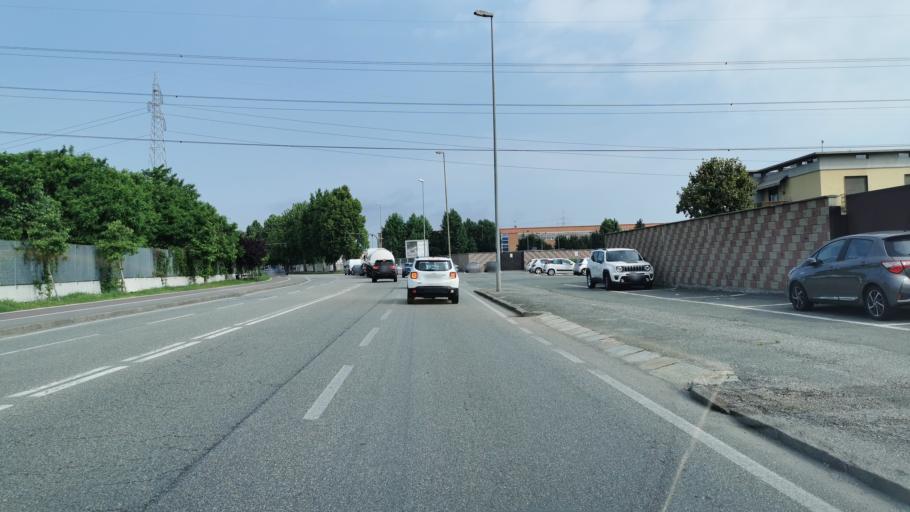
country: IT
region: Piedmont
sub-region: Provincia di Torino
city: Turin
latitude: 45.1043
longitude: 7.7197
